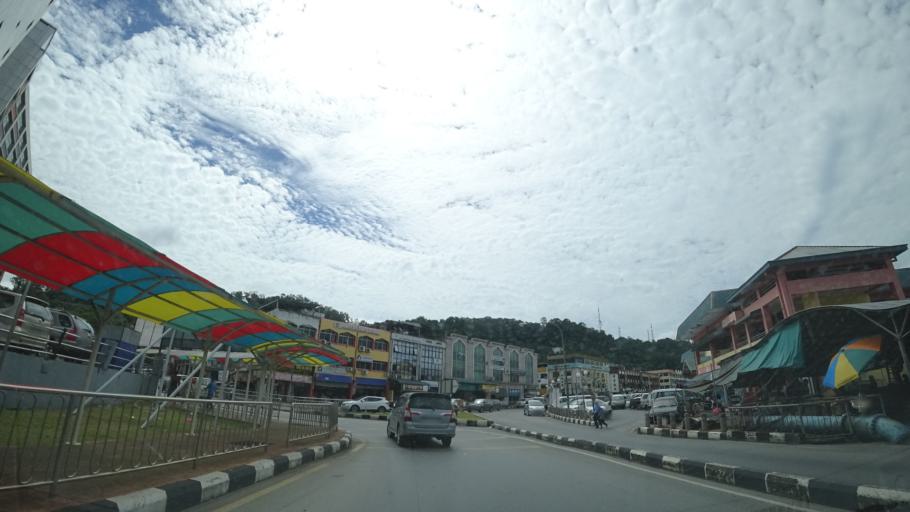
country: MY
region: Sarawak
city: Limbang
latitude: 4.7549
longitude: 115.0088
